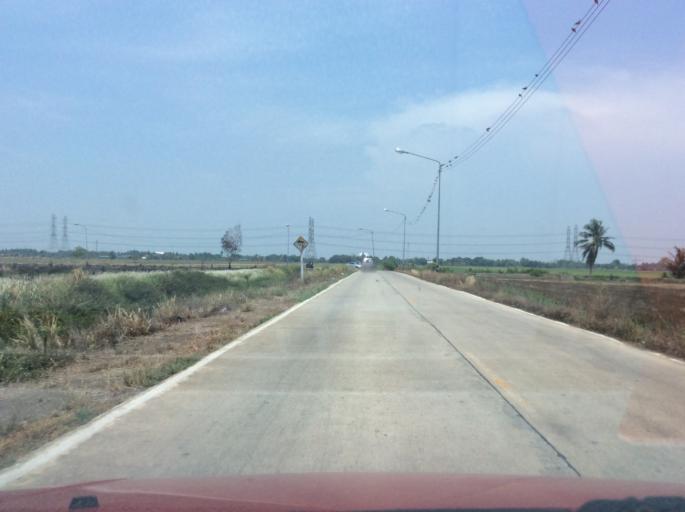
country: TH
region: Pathum Thani
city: Ban Lam Luk Ka
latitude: 13.9843
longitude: 100.7629
